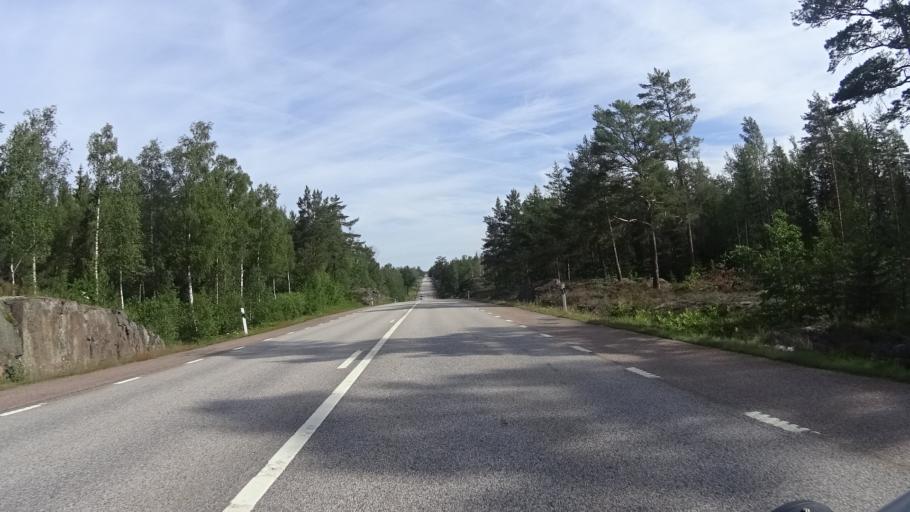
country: SE
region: Kalmar
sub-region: Oskarshamns Kommun
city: Oskarshamn
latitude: 57.4639
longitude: 16.5169
